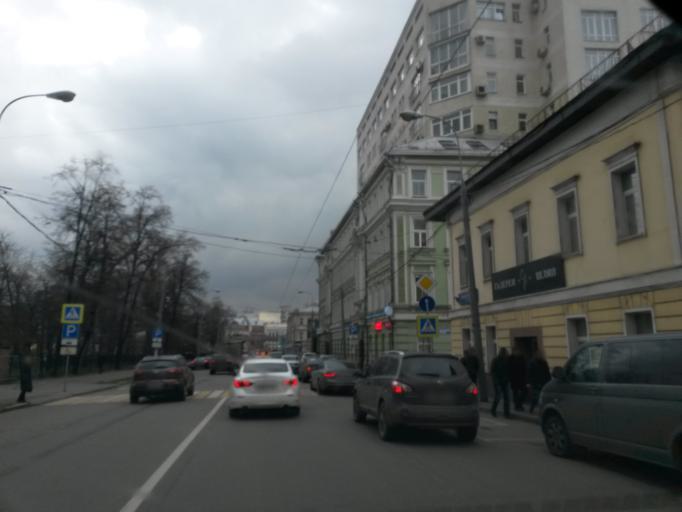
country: RU
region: Moscow
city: Moscow
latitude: 55.7758
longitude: 37.6186
